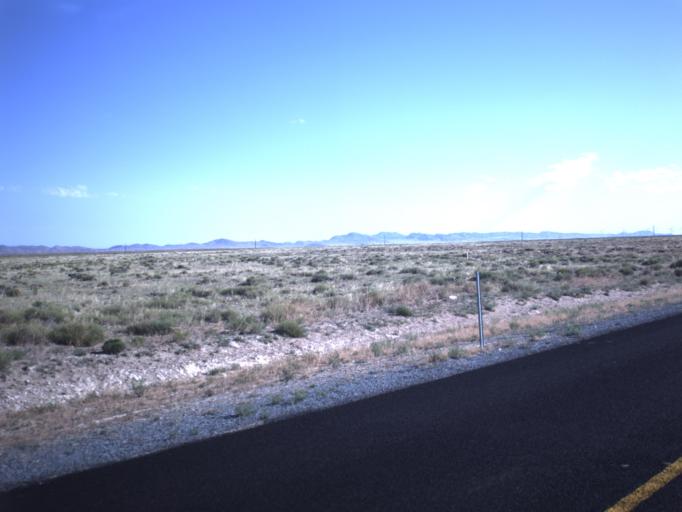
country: US
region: Utah
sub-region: Beaver County
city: Milford
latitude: 38.4657
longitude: -112.9995
